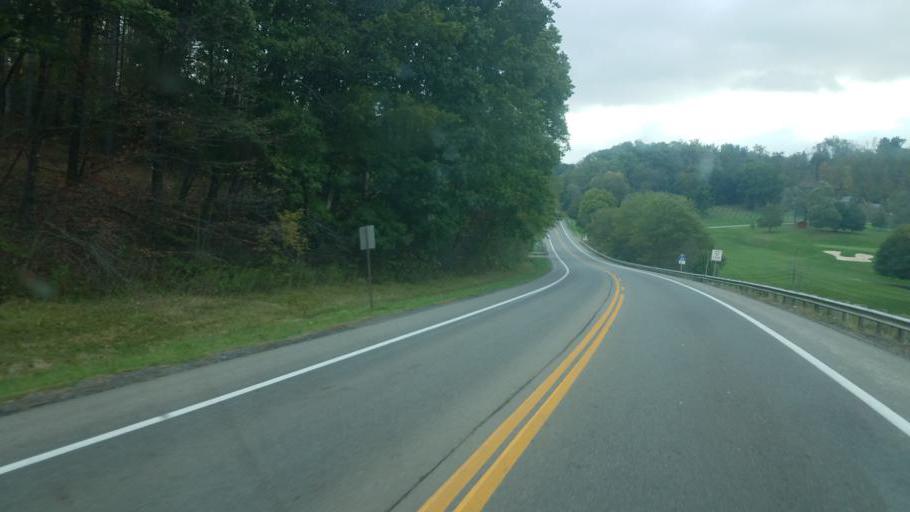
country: US
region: Ohio
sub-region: Holmes County
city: Millersburg
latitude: 40.5555
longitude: -81.9004
